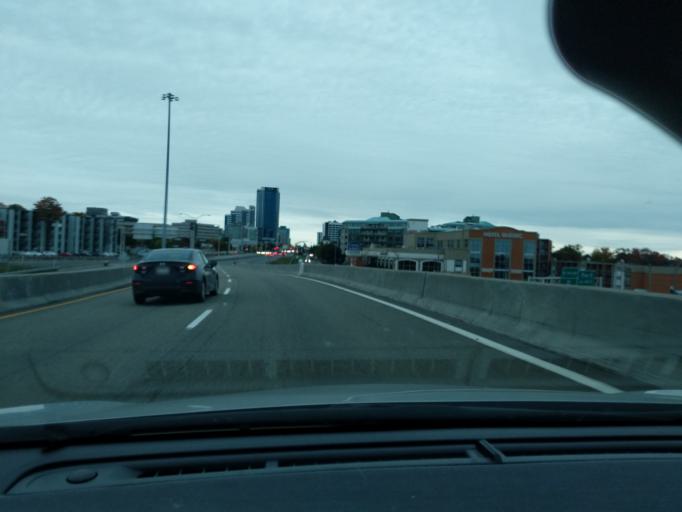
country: CA
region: Quebec
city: L'Ancienne-Lorette
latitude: 46.7619
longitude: -71.2979
